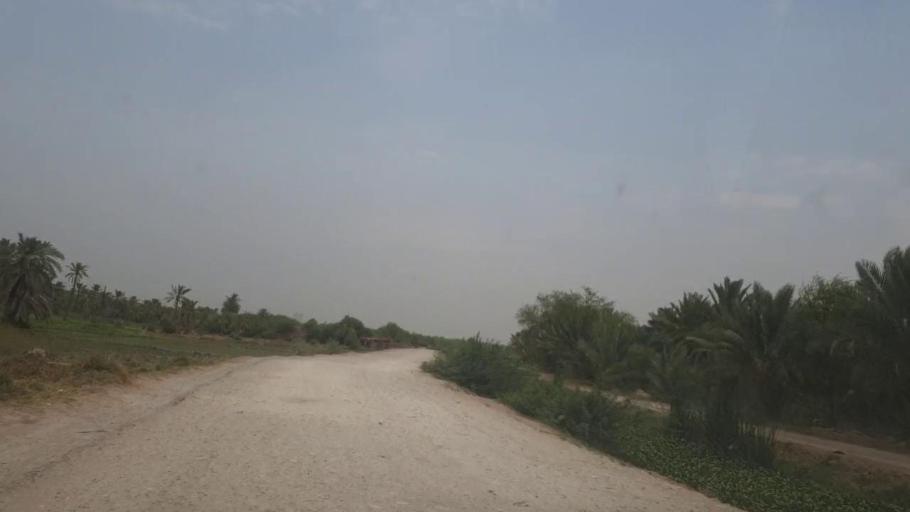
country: PK
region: Sindh
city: Kot Diji
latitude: 27.4265
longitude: 68.6773
